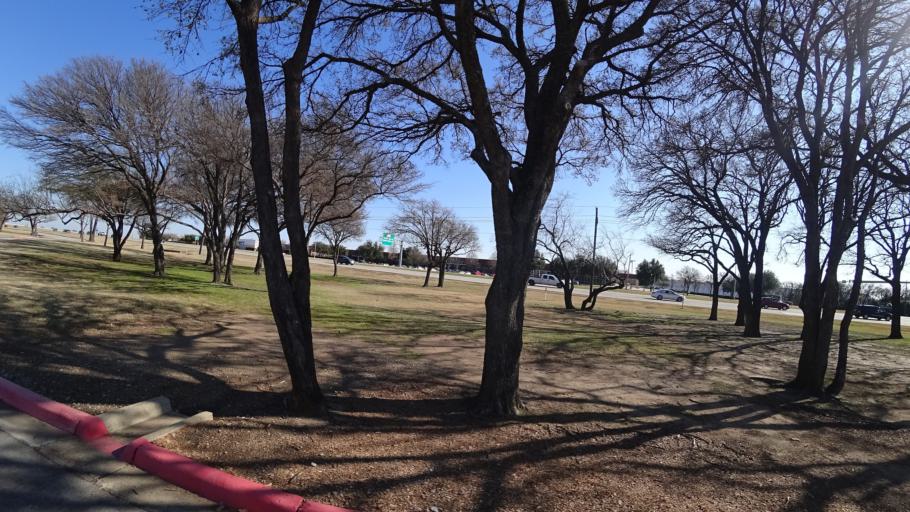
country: US
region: Texas
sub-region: Dallas County
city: Coppell
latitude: 32.9982
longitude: -96.9995
